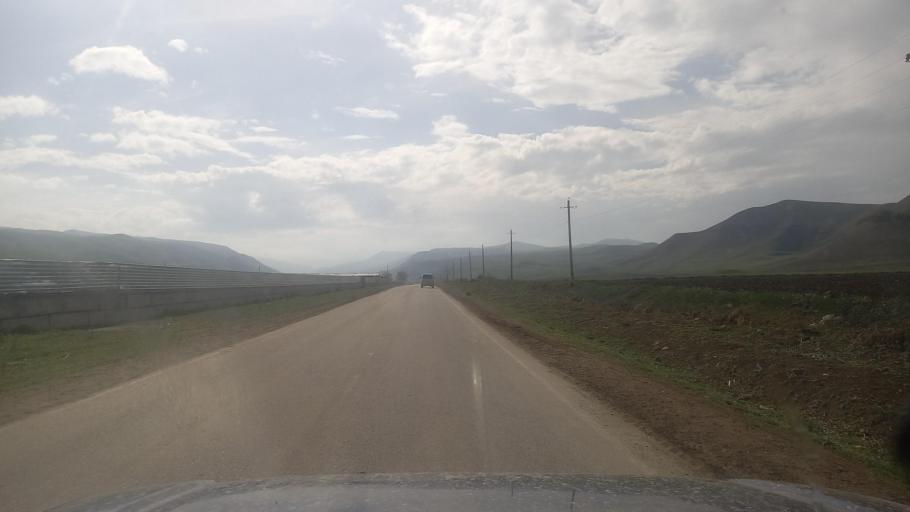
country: RU
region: Kabardino-Balkariya
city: Kamennomostskoye
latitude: 43.7359
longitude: 43.0125
